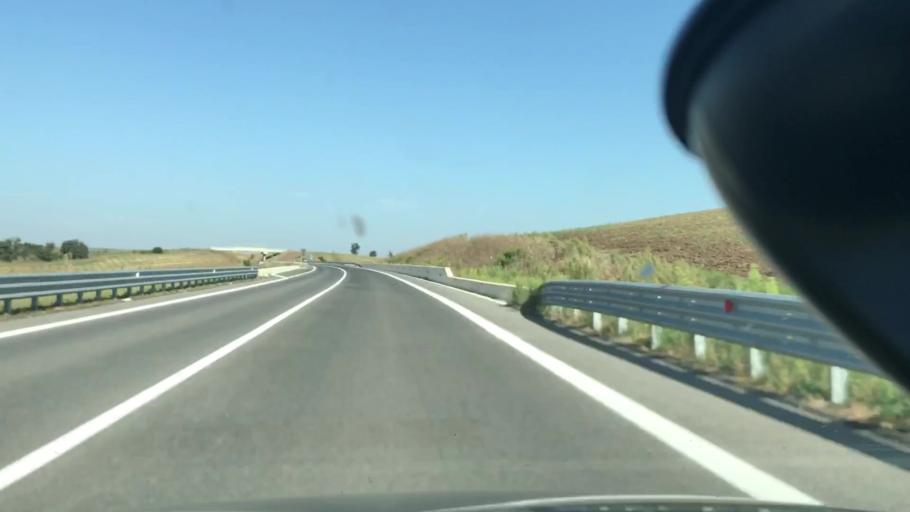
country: IT
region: Basilicate
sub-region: Provincia di Potenza
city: Palazzo San Gervasio
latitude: 40.9645
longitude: 16.0099
